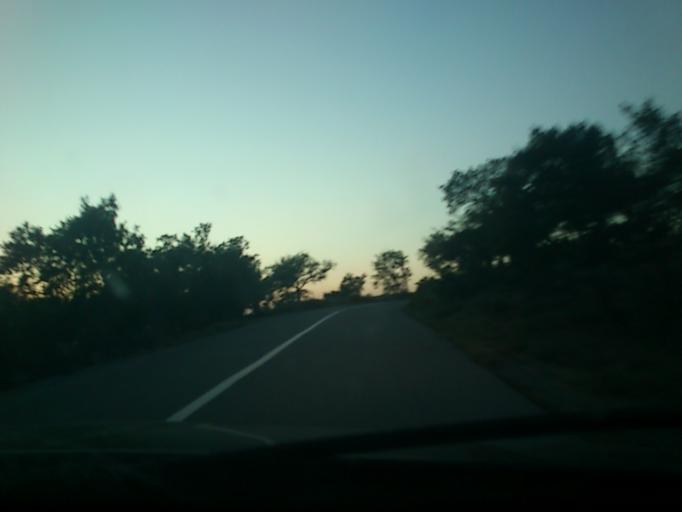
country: HR
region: Licko-Senjska
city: Senj
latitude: 44.9166
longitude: 14.9381
